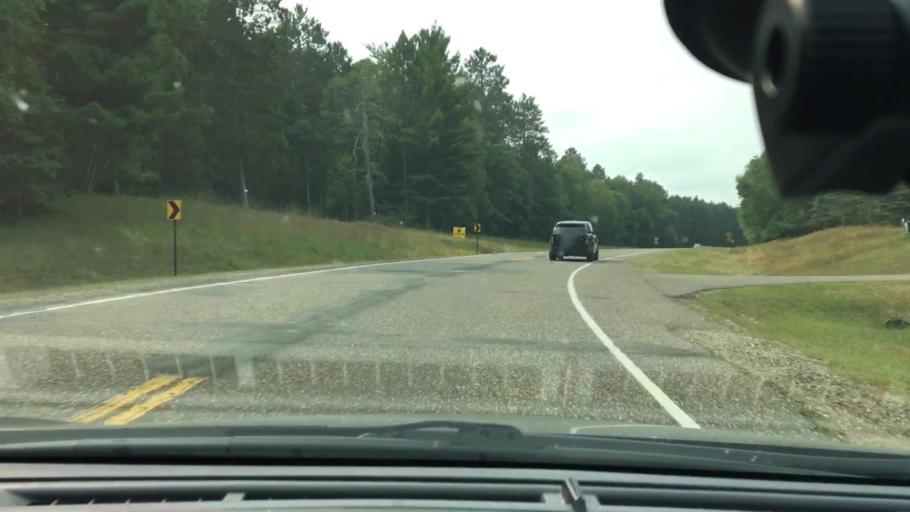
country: US
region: Minnesota
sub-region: Crow Wing County
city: Cross Lake
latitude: 46.6528
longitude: -94.0979
